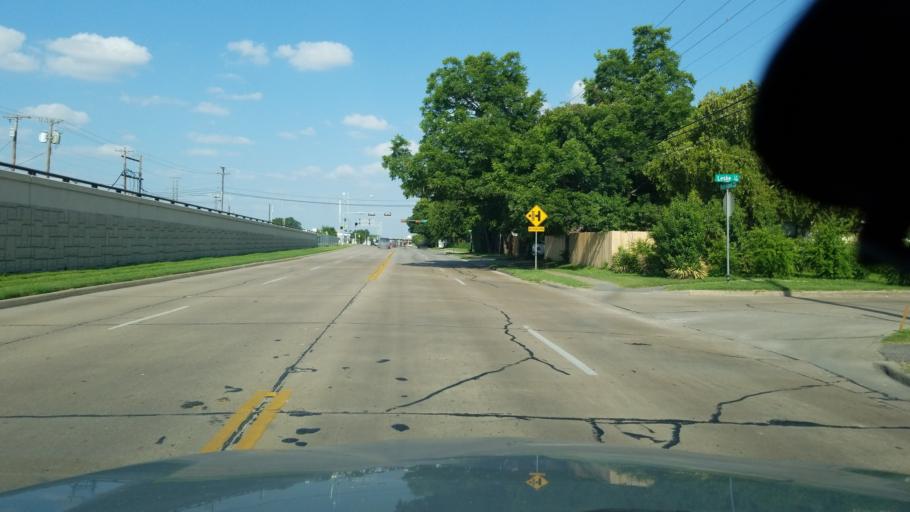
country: US
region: Texas
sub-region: Dallas County
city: Irving
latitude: 32.8152
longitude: -96.9695
